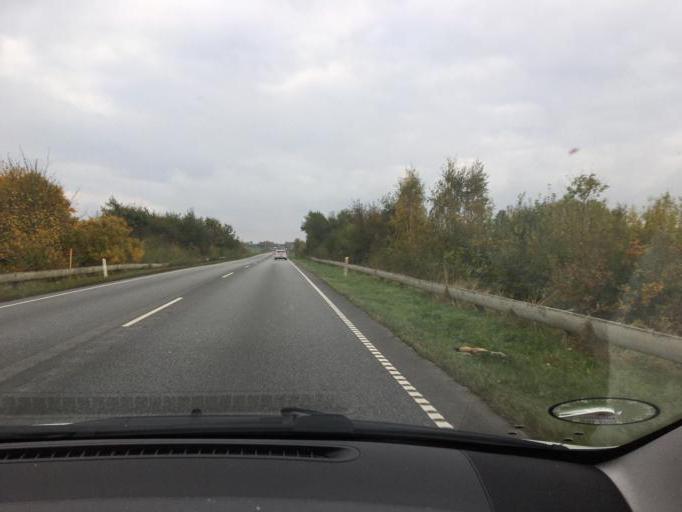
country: DK
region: South Denmark
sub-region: Fredericia Kommune
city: Fredericia
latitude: 55.6151
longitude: 9.7498
